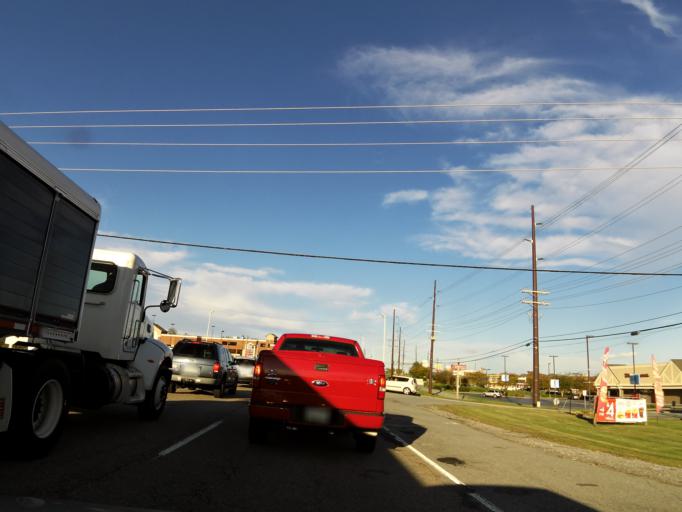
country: US
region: Tennessee
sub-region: Blount County
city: Louisville
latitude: 35.8601
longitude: -84.0705
